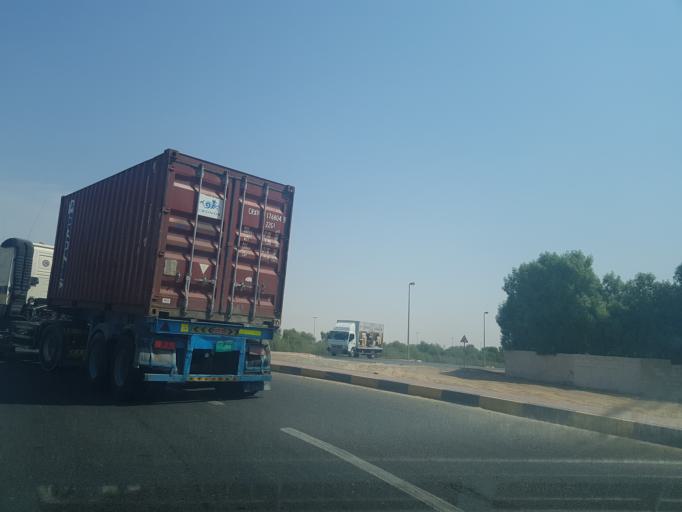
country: AE
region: Ash Shariqah
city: Sharjah
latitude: 25.3126
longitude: 55.5438
